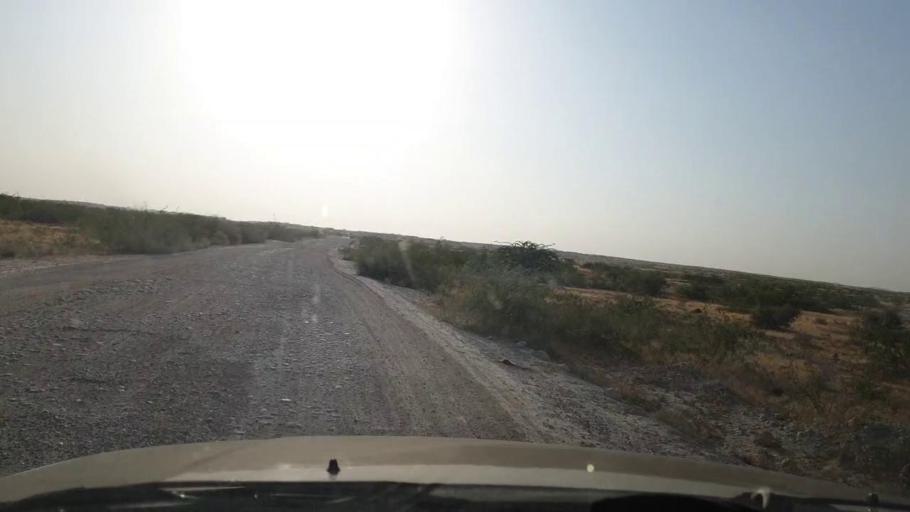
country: PK
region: Sindh
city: Kotri
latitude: 25.2162
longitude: 68.2304
